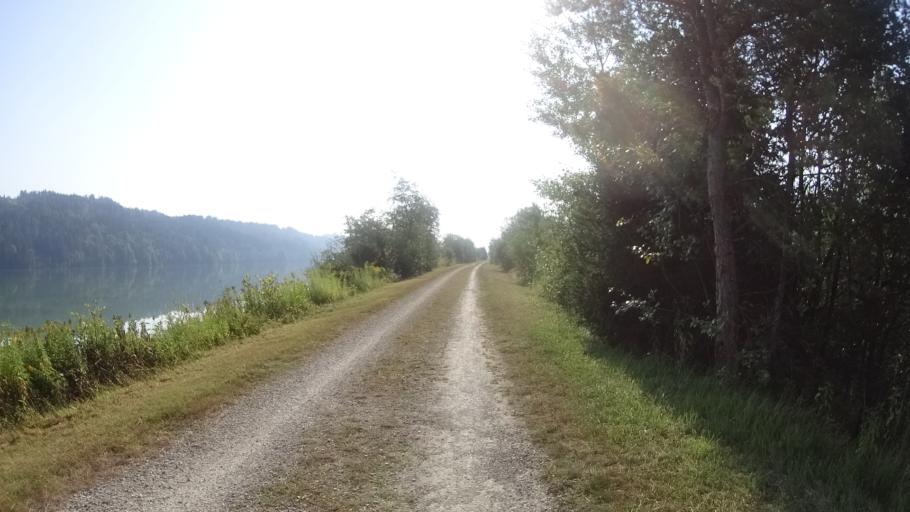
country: AT
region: Carinthia
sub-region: Politischer Bezirk Klagenfurt Land
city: Kottmannsdorf
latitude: 46.5450
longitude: 14.2192
